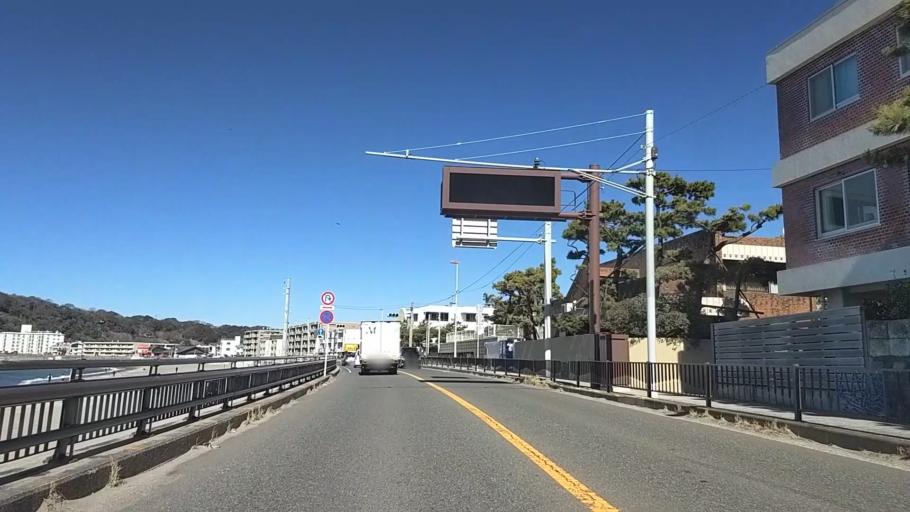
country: JP
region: Kanagawa
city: Zushi
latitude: 35.2897
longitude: 139.5740
